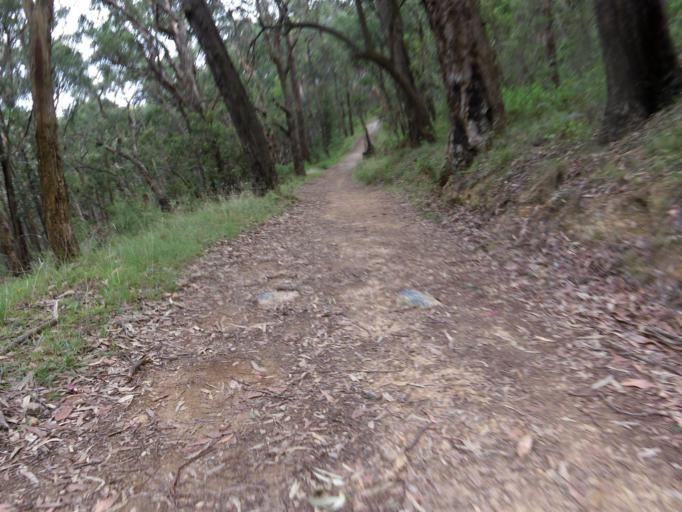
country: AU
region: Victoria
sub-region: Knox
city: The Basin
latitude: -37.8392
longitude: 145.3382
